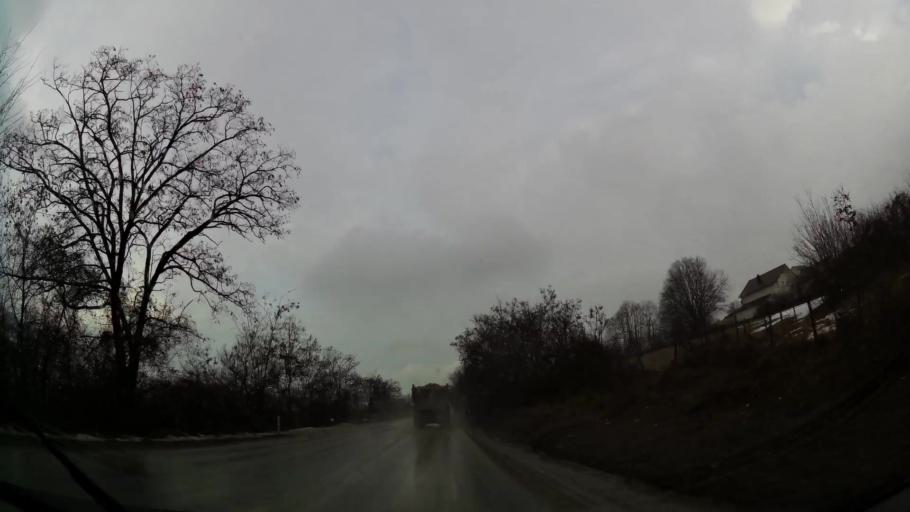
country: XK
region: Ferizaj
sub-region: Komuna e Kacanikut
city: Kacanik
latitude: 42.2374
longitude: 21.2468
